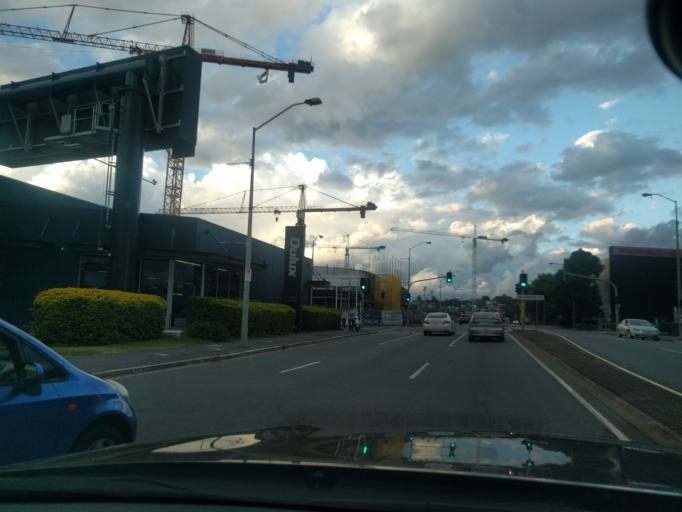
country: AU
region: Queensland
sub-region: Brisbane
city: Windsor
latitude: -27.4445
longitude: 153.0432
